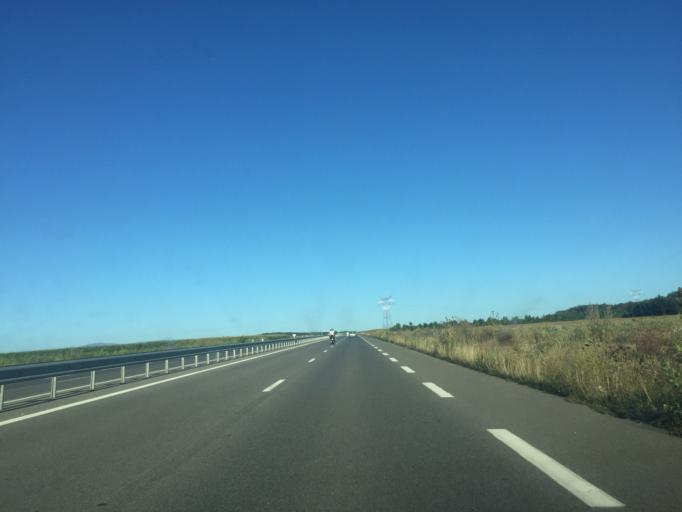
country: FR
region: Rhone-Alpes
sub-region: Departement de l'Isere
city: Janneyrias
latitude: 45.7662
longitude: 5.1014
